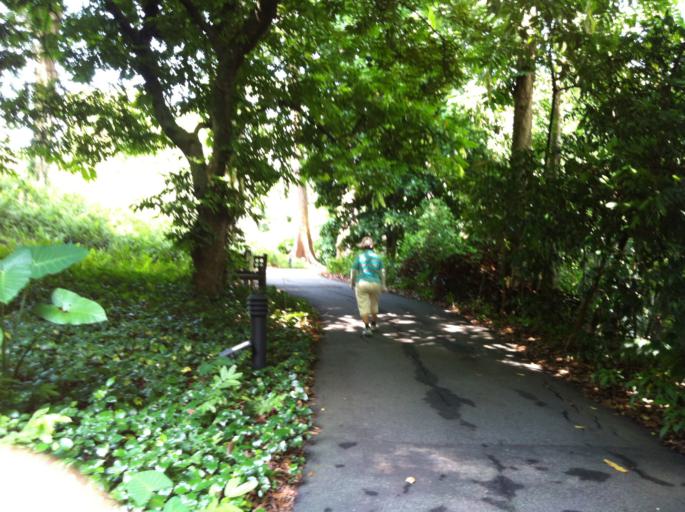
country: SG
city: Singapore
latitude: 1.3160
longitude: 103.8152
